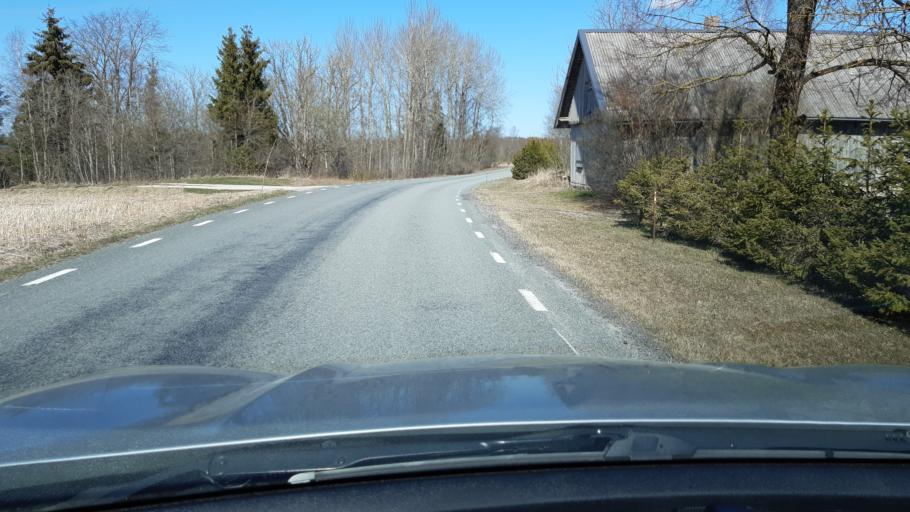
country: EE
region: Raplamaa
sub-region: Kohila vald
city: Kohila
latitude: 59.1888
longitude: 24.8734
